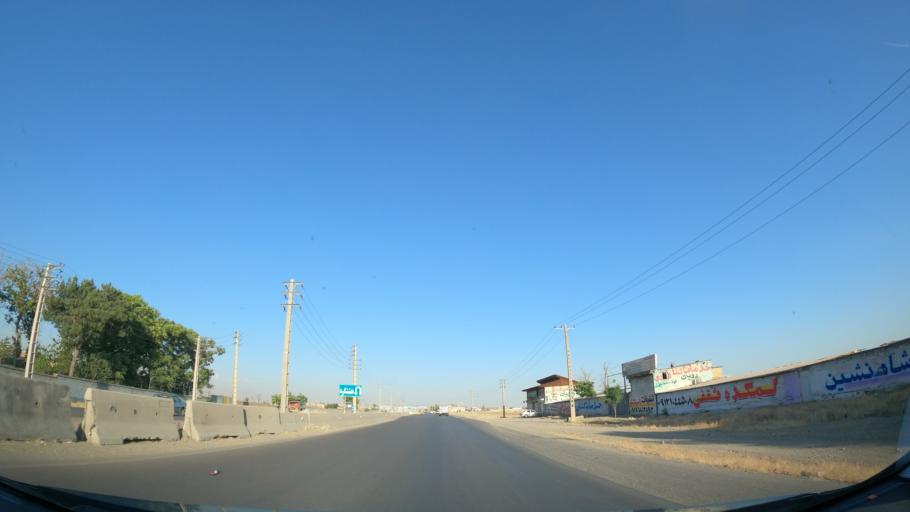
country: IR
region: Alborz
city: Hashtgerd
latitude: 35.9210
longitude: 50.7468
